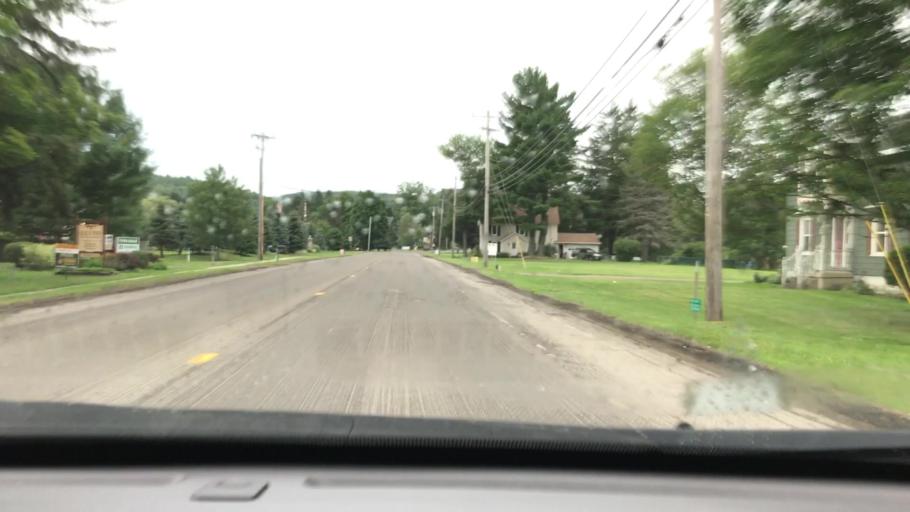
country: US
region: New York
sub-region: Cattaraugus County
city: Salamanca
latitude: 42.2816
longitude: -78.6645
